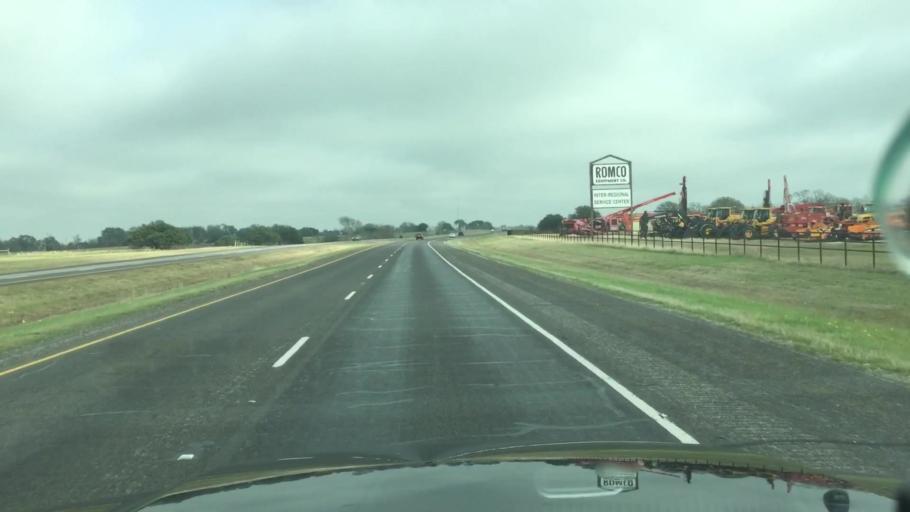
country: US
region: Texas
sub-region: Burleson County
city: Somerville
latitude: 30.1510
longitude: -96.6697
